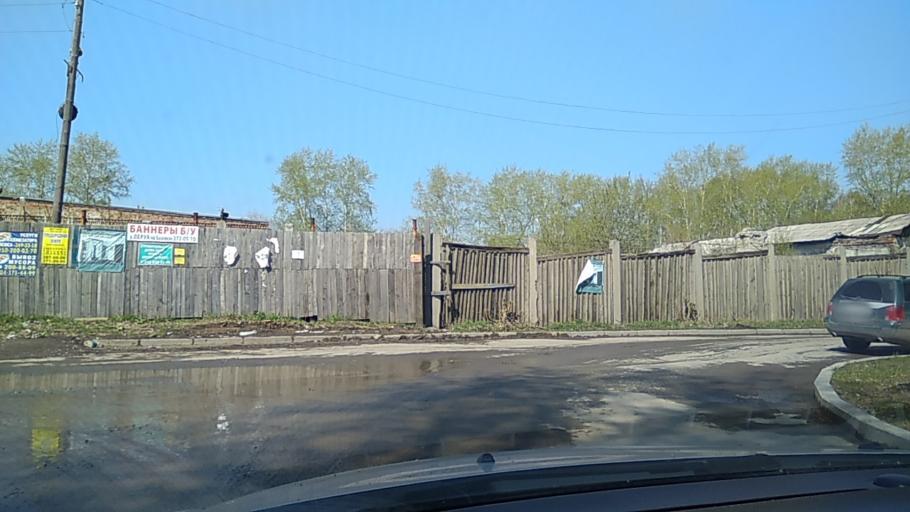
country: RU
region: Sverdlovsk
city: Verkhnyaya Pyshma
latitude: 56.9104
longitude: 60.5834
